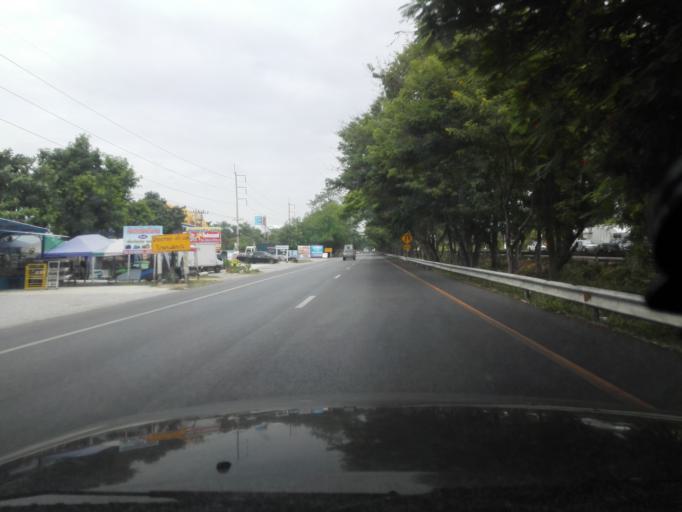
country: TH
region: Nakhon Sawan
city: Nakhon Sawan
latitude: 15.7317
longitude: 100.0318
